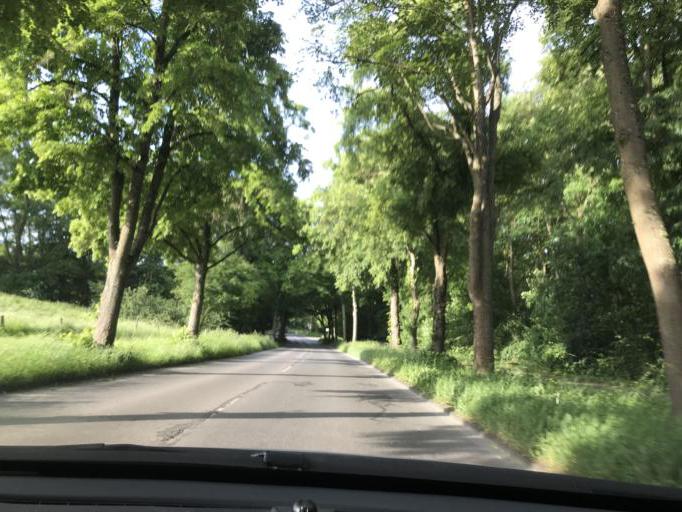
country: DE
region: North Rhine-Westphalia
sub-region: Regierungsbezirk Koln
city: Aachen
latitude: 50.7527
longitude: 6.1300
